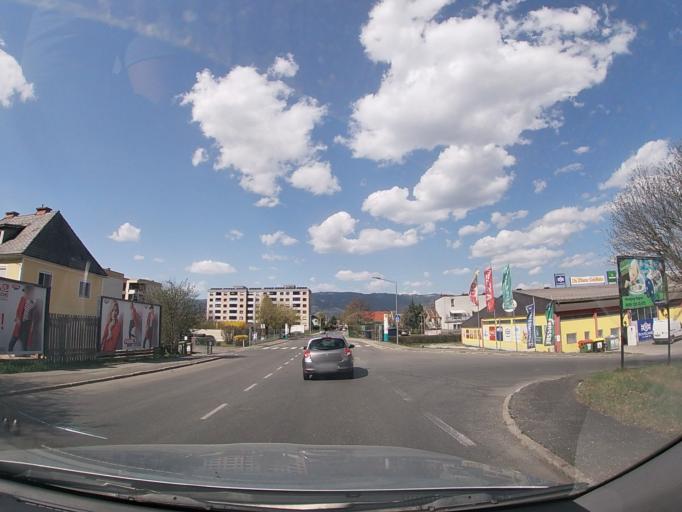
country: AT
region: Styria
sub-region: Politischer Bezirk Murtal
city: Judenburg
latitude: 47.1683
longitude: 14.6795
